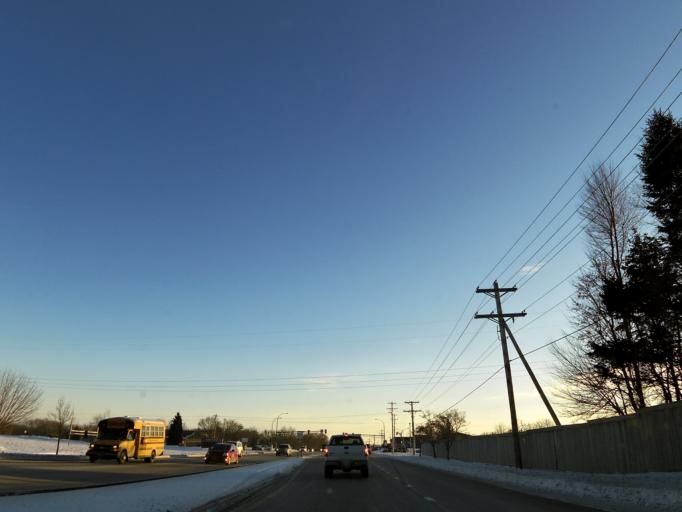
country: US
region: Minnesota
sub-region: Carver County
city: Chaska
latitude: 44.8069
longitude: -93.6020
